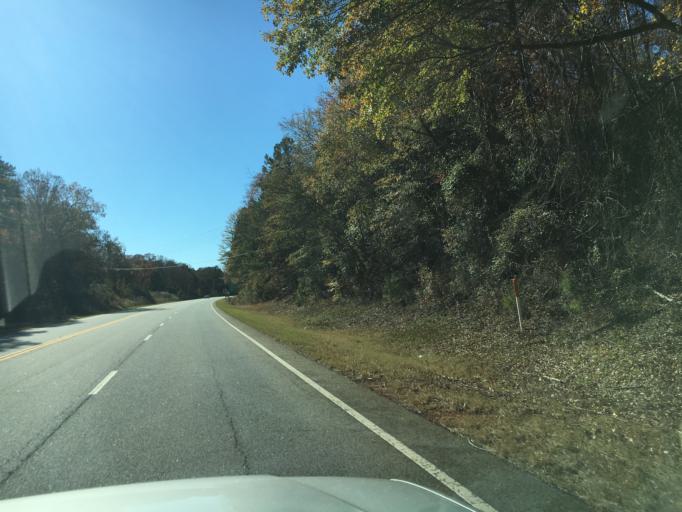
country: US
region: Georgia
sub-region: Hart County
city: Hartwell
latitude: 34.3493
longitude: -82.8195
